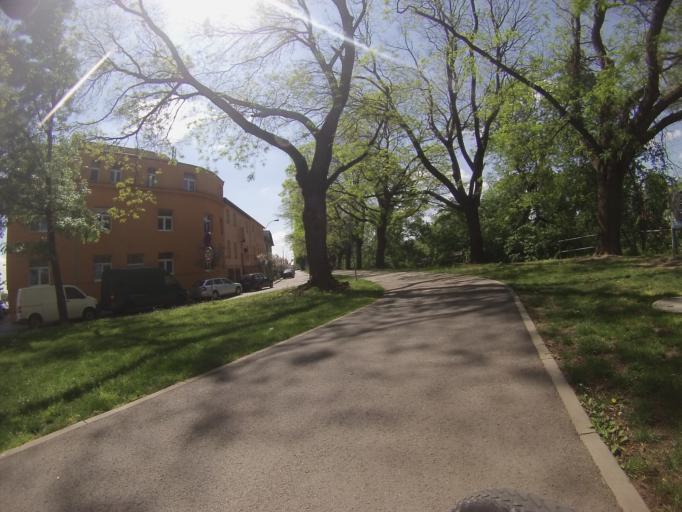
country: CZ
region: South Moravian
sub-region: Mesto Brno
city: Brno
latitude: 49.1768
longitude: 16.6180
